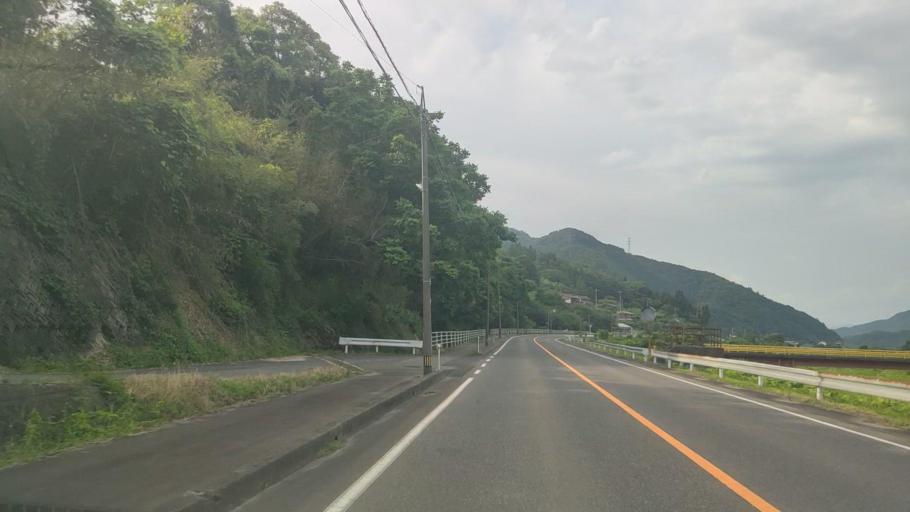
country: JP
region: Tottori
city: Kurayoshi
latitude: 35.3436
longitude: 133.8410
